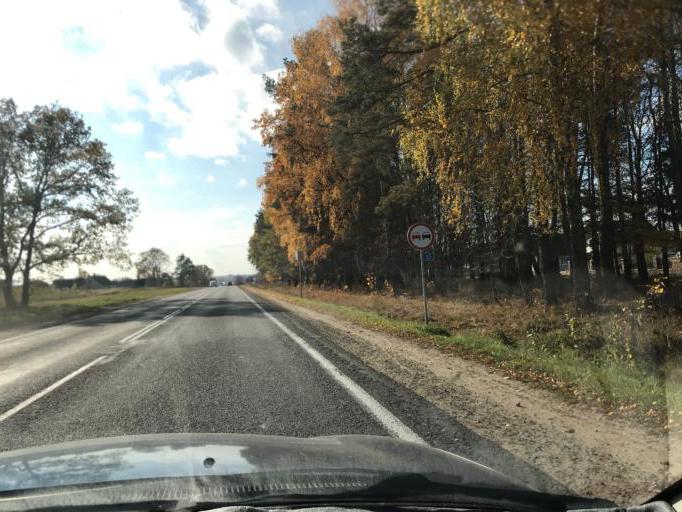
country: BY
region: Grodnenskaya
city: Voranava
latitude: 54.1639
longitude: 25.3288
